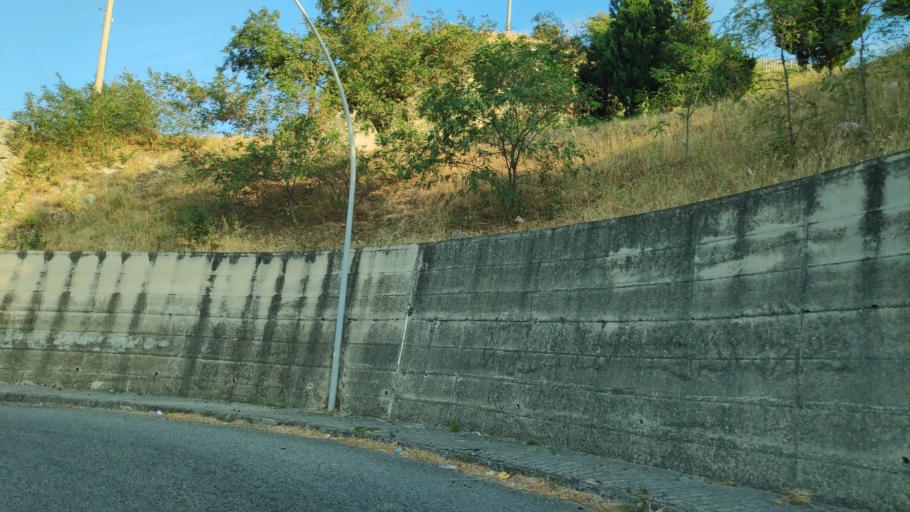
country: IT
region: Calabria
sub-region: Provincia di Catanzaro
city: Satriano
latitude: 38.6703
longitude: 16.4816
